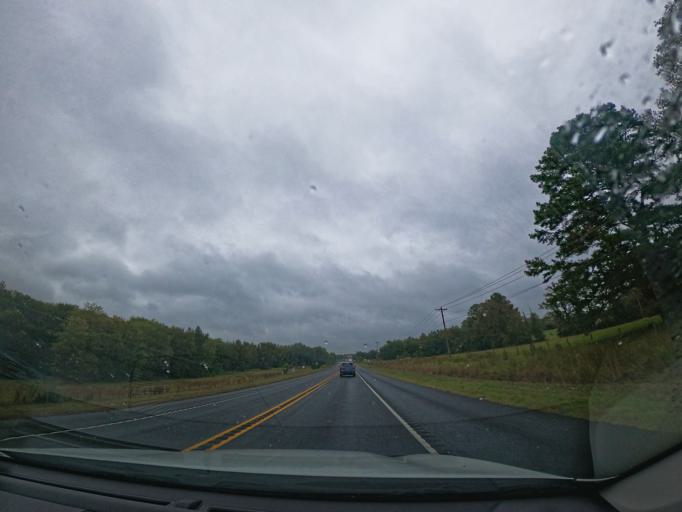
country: US
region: Louisiana
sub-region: Caddo Parish
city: Greenwood
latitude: 32.4395
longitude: -93.9826
